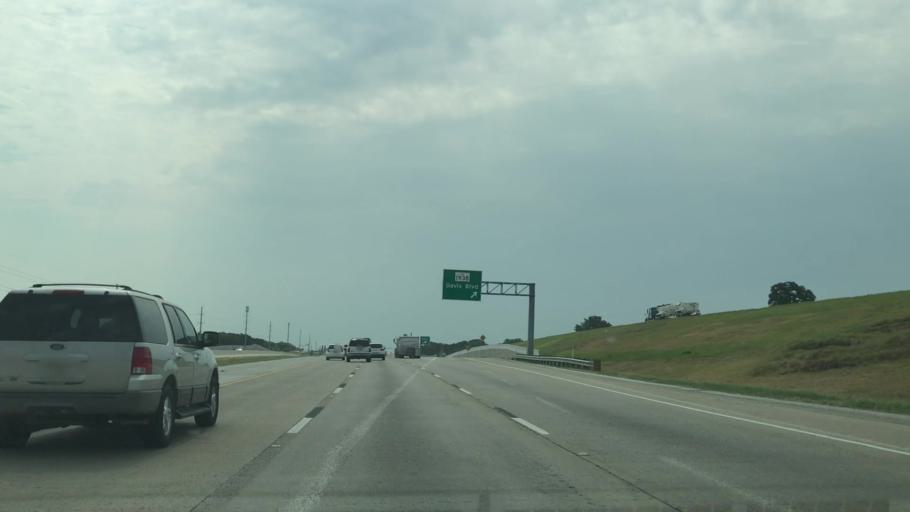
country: US
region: Texas
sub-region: Denton County
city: Trophy Club
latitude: 32.9924
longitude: -97.1924
